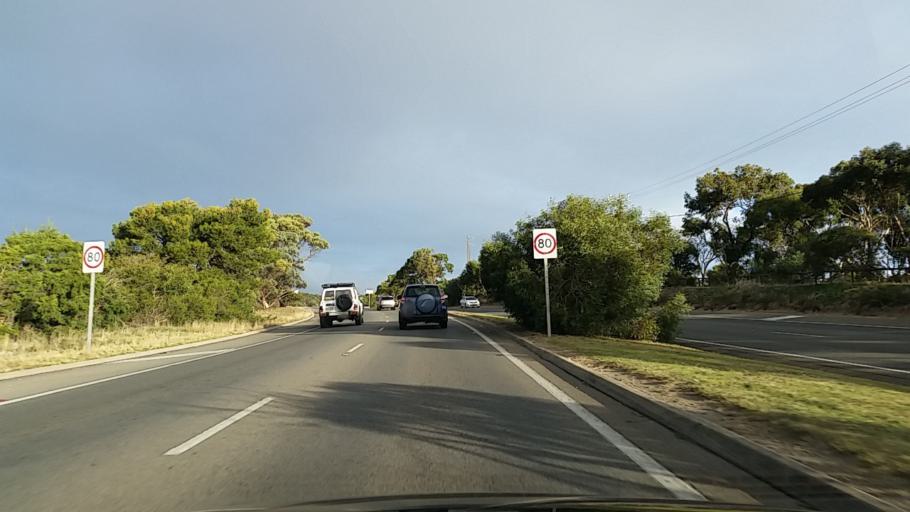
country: AU
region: South Australia
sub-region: Adelaide Hills
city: Seacliff
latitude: -35.0468
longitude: 138.5320
